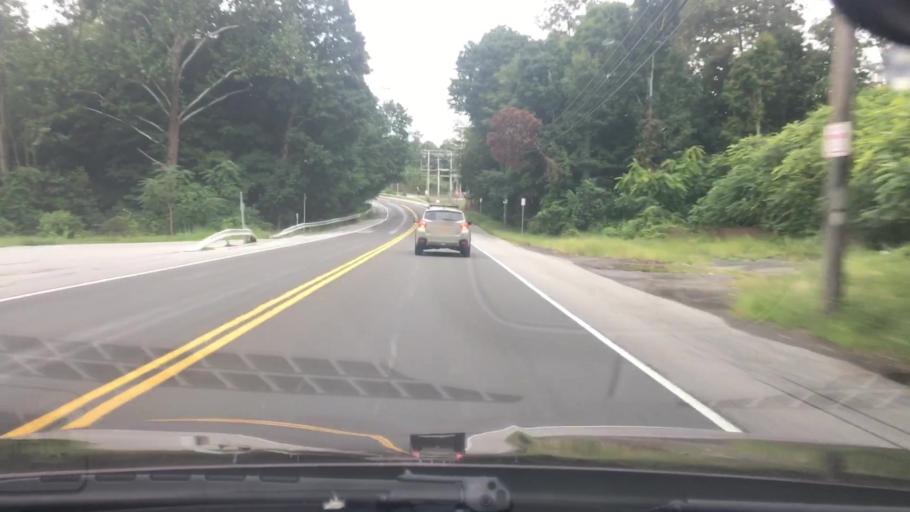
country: US
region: New York
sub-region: Dutchess County
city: Pleasant Valley
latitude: 41.7413
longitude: -73.8310
